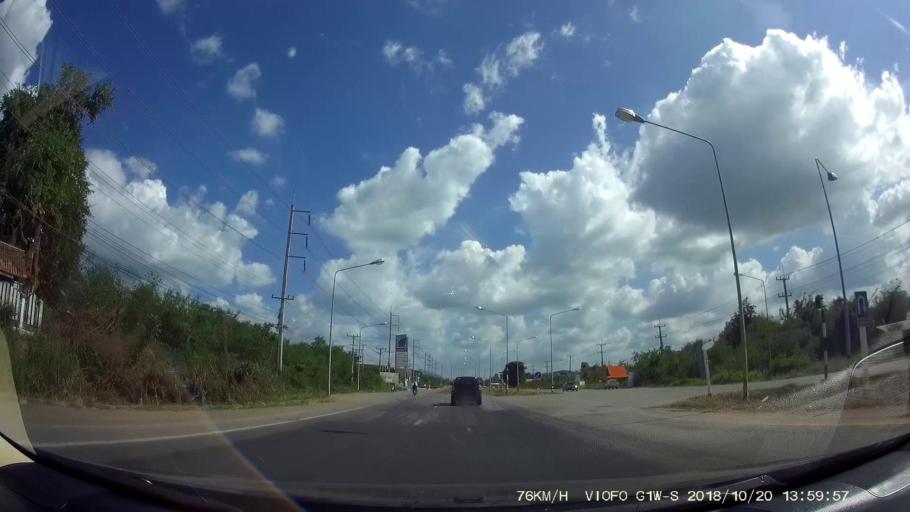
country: TH
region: Khon Kaen
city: Chum Phae
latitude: 16.5197
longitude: 102.1162
